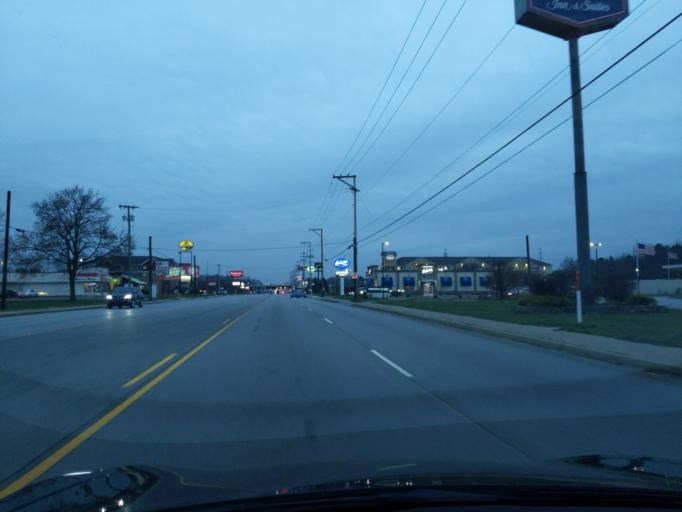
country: US
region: Indiana
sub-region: Saint Joseph County
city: Georgetown
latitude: 41.7269
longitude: -86.2506
